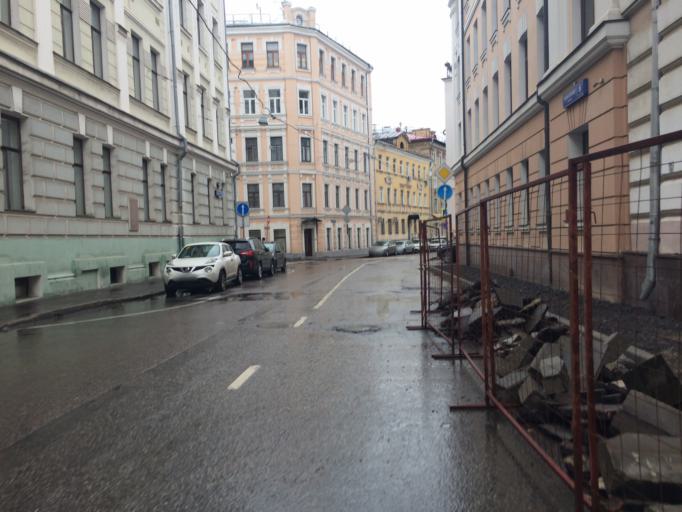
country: RU
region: Moscow
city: Zamoskvorech'ye
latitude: 55.7616
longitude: 37.6477
